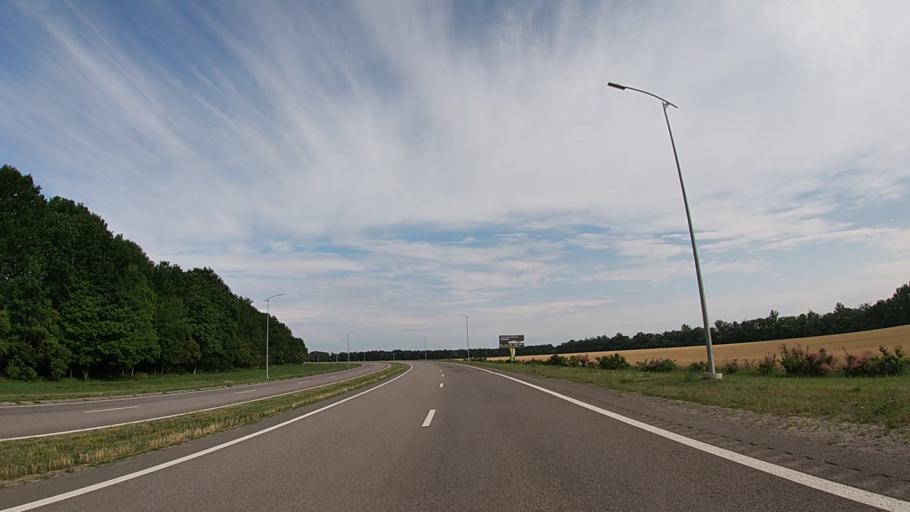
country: RU
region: Belgorod
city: Borisovka
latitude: 50.7590
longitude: 35.9643
